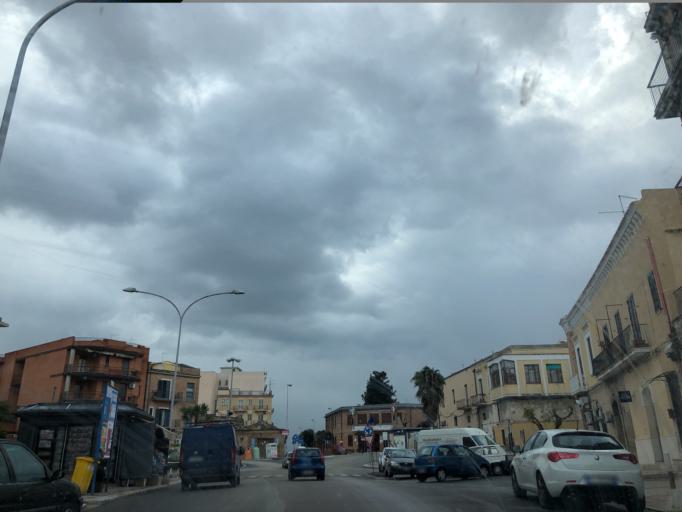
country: IT
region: Apulia
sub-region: Provincia di Foggia
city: Lucera
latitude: 41.5060
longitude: 15.3388
